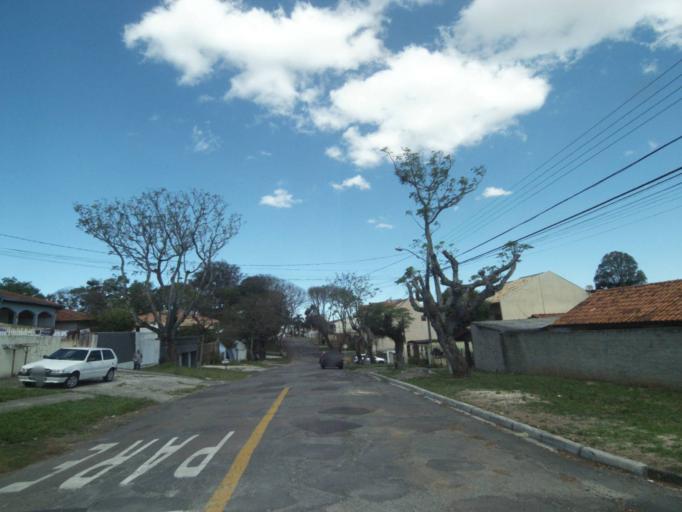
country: BR
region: Parana
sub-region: Curitiba
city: Curitiba
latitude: -25.3781
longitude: -49.2443
